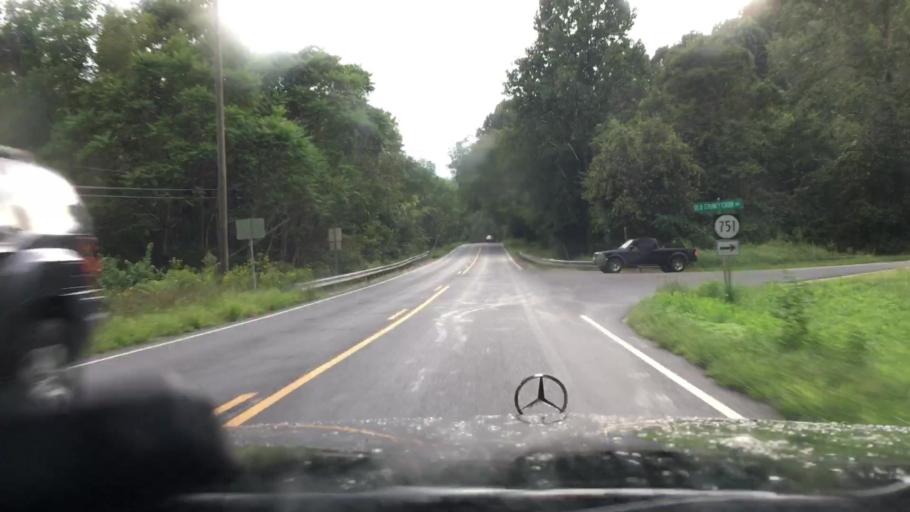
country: US
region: Virginia
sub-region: Nelson County
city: Nellysford
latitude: 37.8864
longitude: -78.8942
